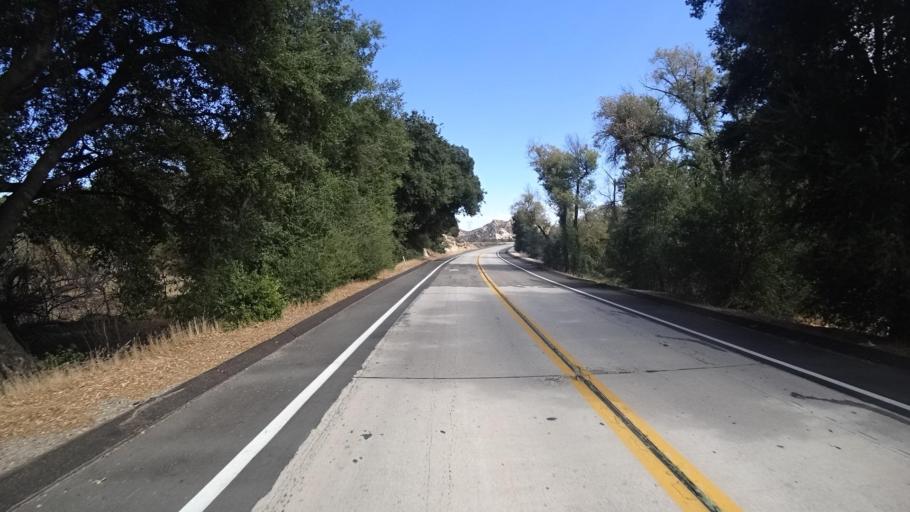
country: MX
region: Baja California
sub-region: Tecate
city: Cereso del Hongo
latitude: 32.6606
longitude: -116.2527
